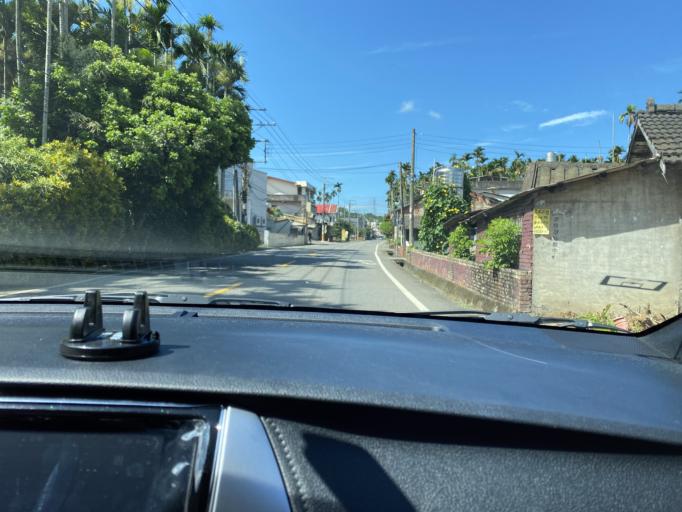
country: TW
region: Taiwan
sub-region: Nantou
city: Nantou
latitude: 23.8600
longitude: 120.6319
